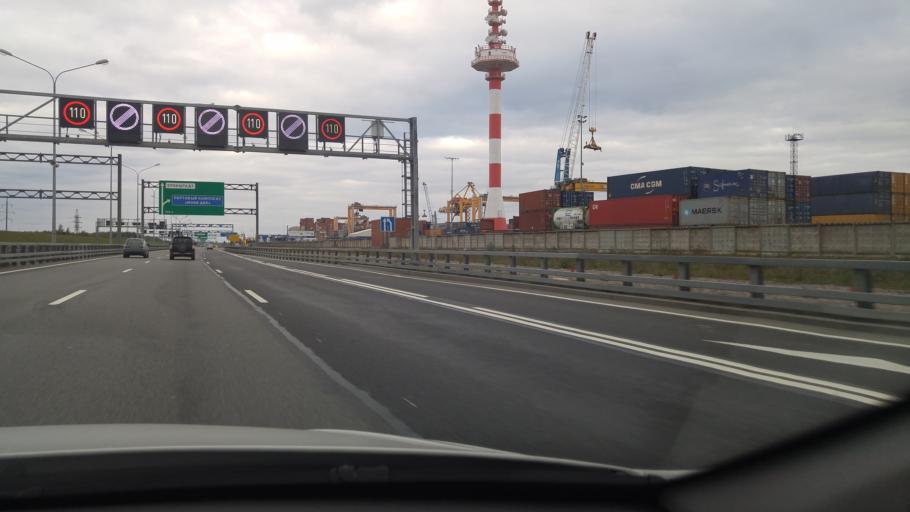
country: RU
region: St.-Petersburg
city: Kronshtadt
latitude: 60.0018
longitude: 29.7040
